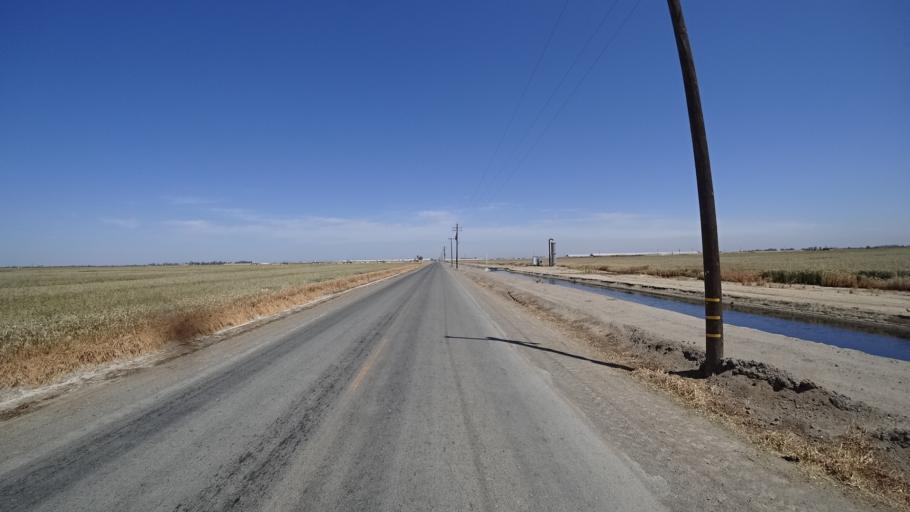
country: US
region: California
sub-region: Kings County
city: Home Garden
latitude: 36.1916
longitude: -119.6906
